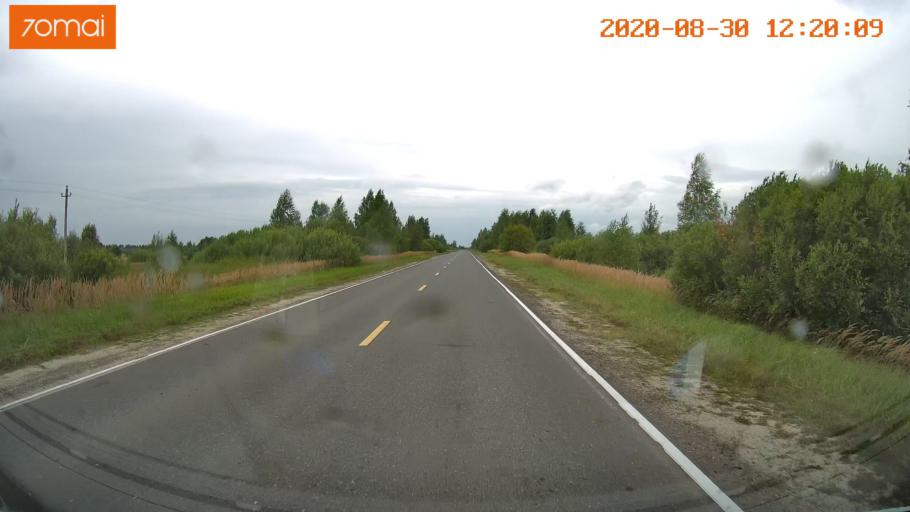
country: RU
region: Ivanovo
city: Yur'yevets
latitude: 57.3229
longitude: 42.9086
